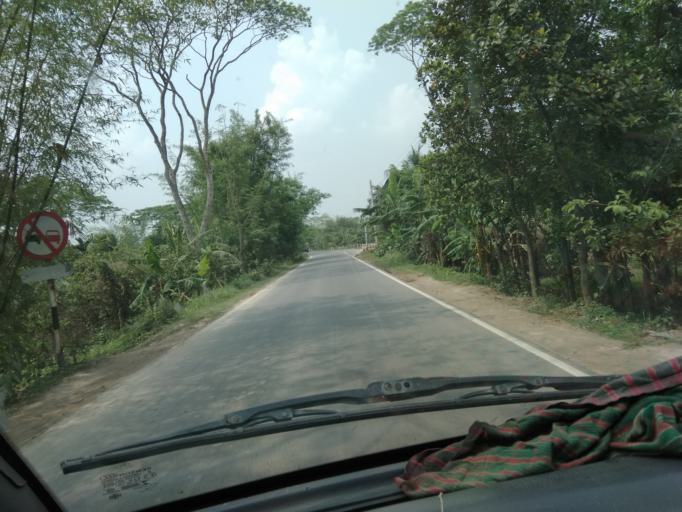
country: BD
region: Dhaka
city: Char Bhadrasan
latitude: 23.4064
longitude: 90.2172
